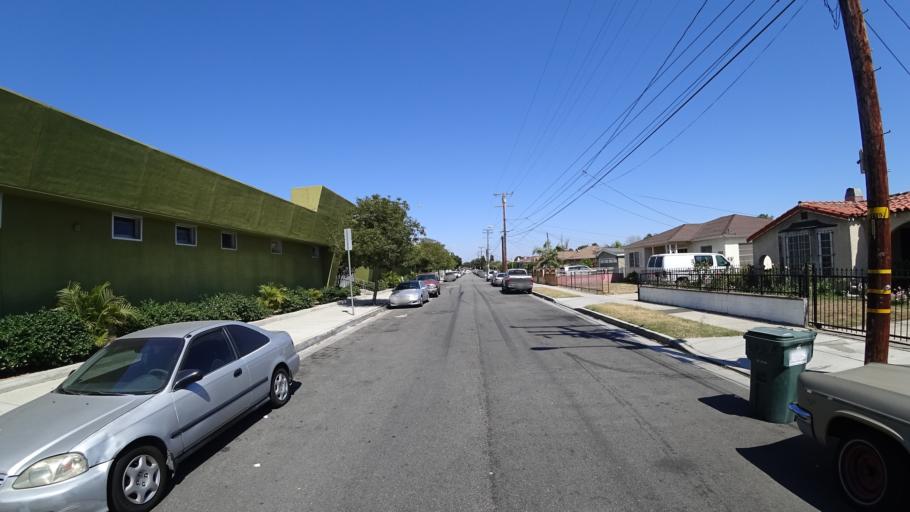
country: US
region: California
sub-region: Los Angeles County
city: Lennox
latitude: 33.9409
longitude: -118.3467
